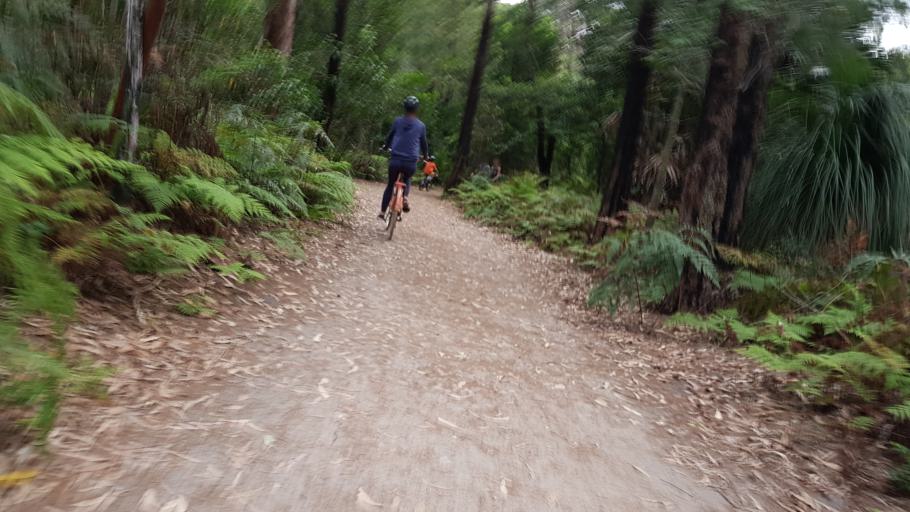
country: AU
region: New South Wales
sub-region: Warringah
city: Narrabeen
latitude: -33.7188
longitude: 151.2800
